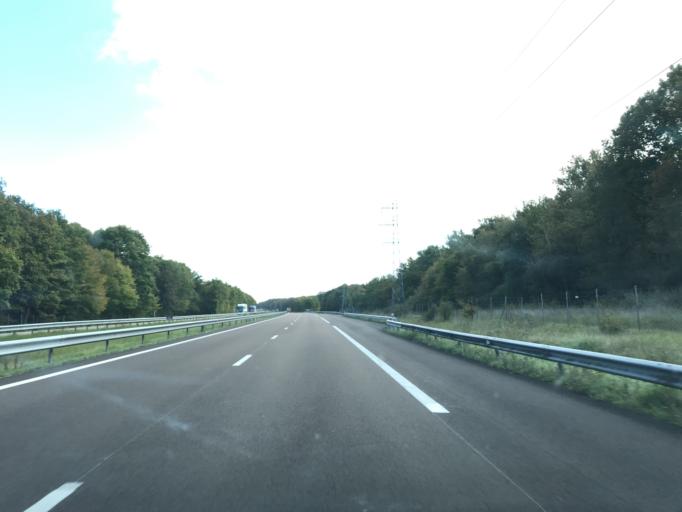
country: FR
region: Centre
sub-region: Departement du Loiret
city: Courtenay
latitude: 48.0851
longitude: 3.0449
